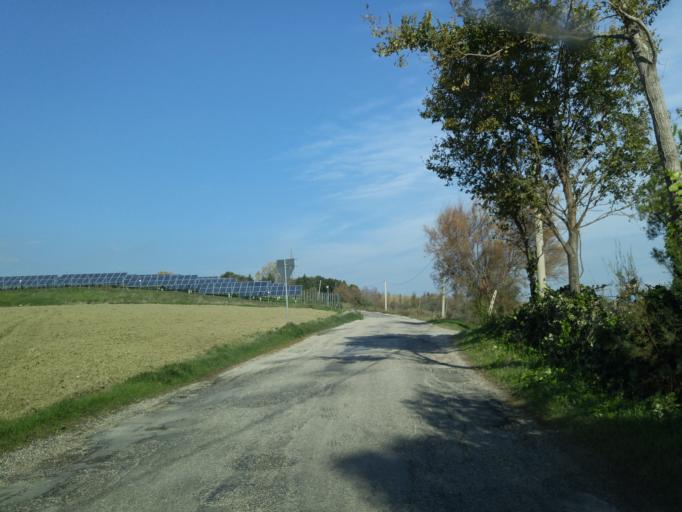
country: IT
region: The Marches
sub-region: Provincia di Pesaro e Urbino
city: Lucrezia
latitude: 43.8027
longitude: 12.9131
